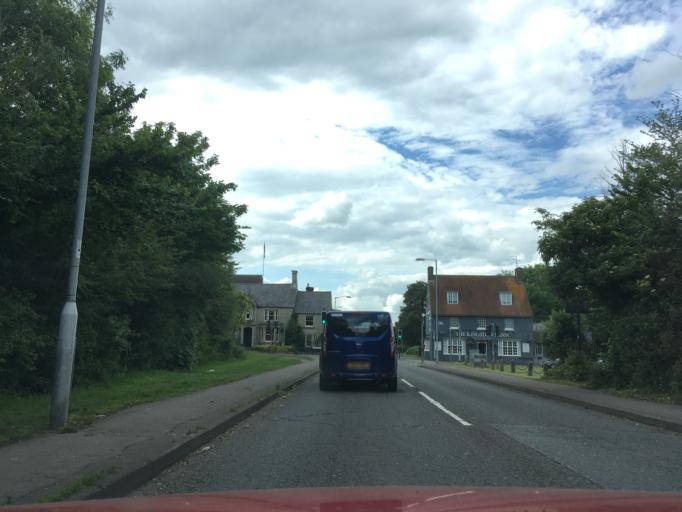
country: GB
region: England
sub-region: Borough of Swindon
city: Broad Blunsdon
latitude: 51.5917
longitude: -1.7611
